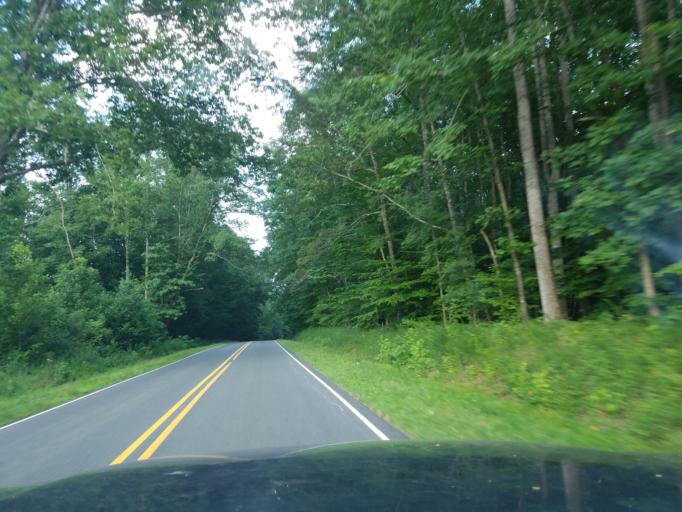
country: US
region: North Carolina
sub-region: Granville County
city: Butner
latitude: 36.2015
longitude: -78.8574
